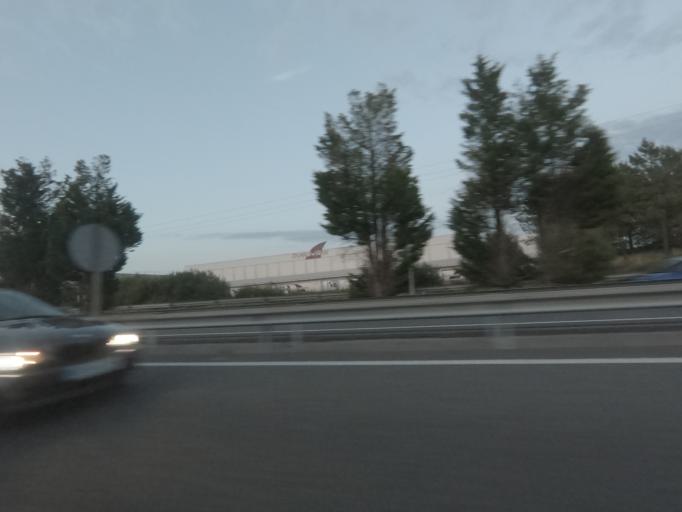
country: ES
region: Galicia
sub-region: Provincia de Pontevedra
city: Porrino
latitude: 42.1065
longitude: -8.6209
